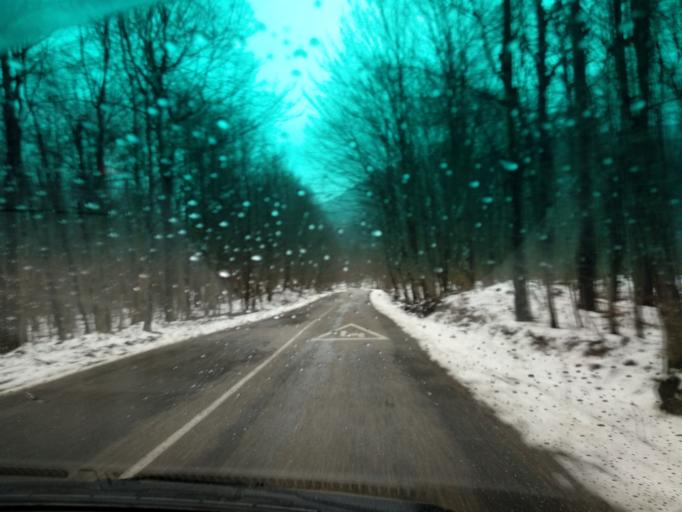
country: RU
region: Krasnodarskiy
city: Khadyzhensk
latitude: 44.2153
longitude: 39.4006
